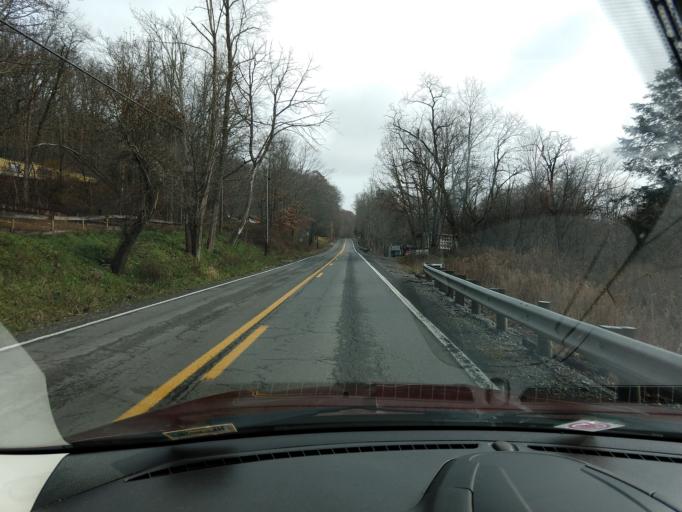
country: US
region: West Virginia
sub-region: Greenbrier County
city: Rainelle
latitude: 38.0995
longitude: -80.6988
